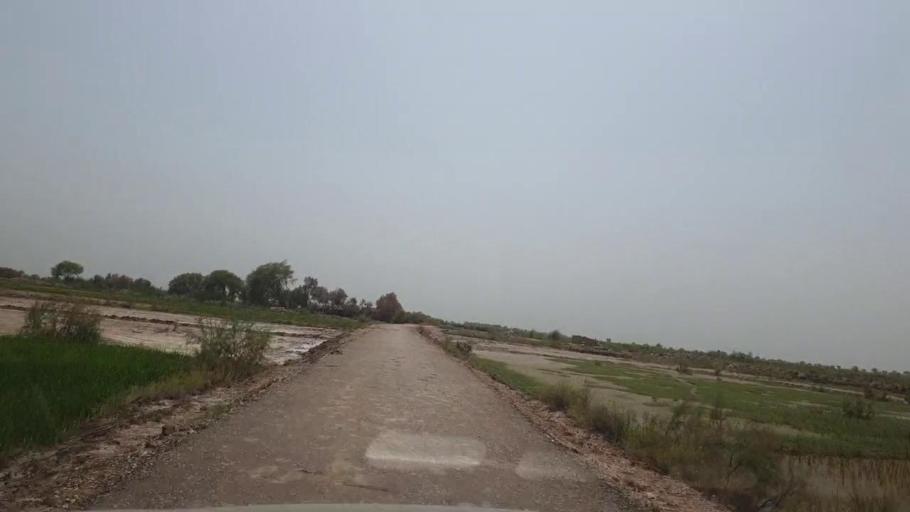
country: PK
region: Sindh
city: Garhi Yasin
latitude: 28.0573
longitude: 68.3164
